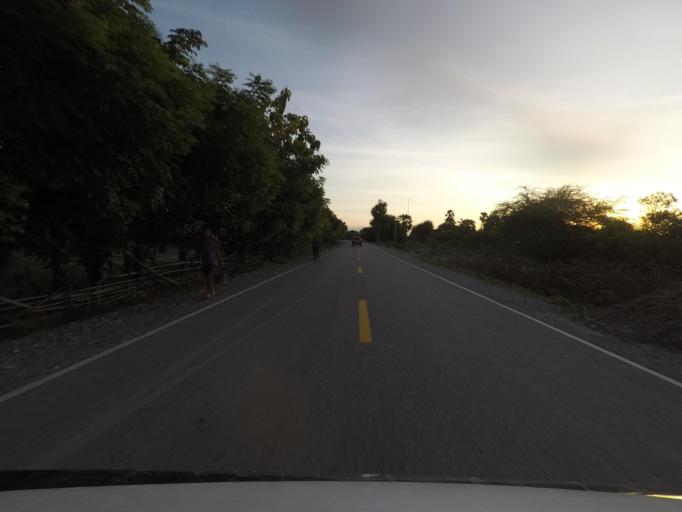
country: TL
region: Baucau
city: Baucau
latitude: -8.4302
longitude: 126.6834
